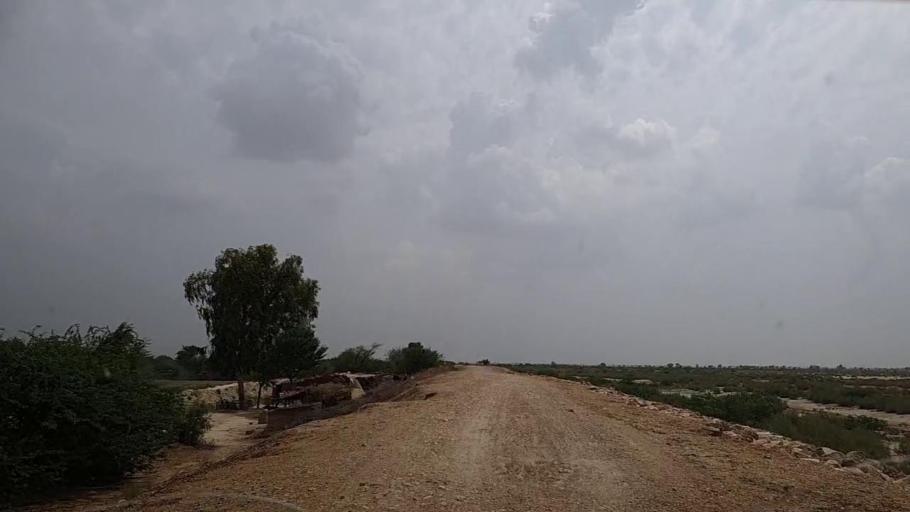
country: PK
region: Sindh
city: Johi
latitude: 26.7347
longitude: 67.5810
